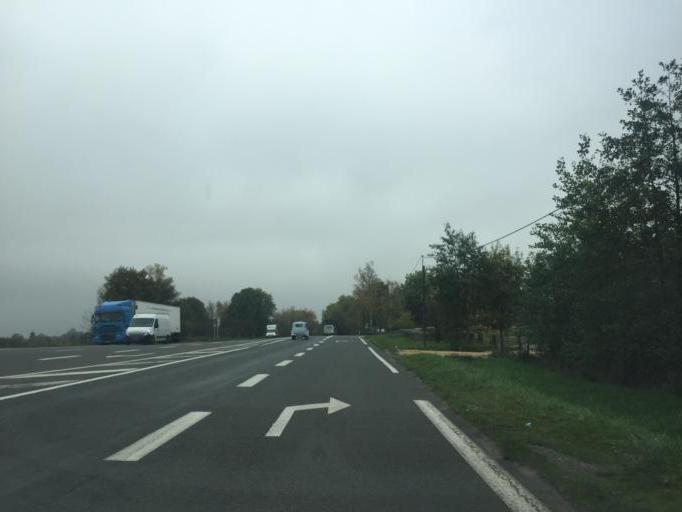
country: FR
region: Rhone-Alpes
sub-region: Departement de l'Ain
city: Villars-les-Dombes
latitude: 45.9915
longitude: 5.0234
